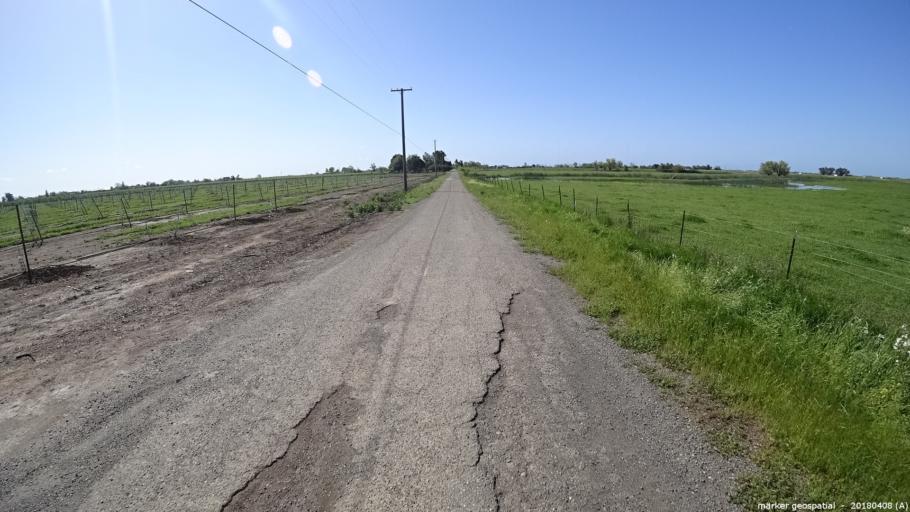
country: US
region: California
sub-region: Sacramento County
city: Laguna
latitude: 38.3454
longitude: -121.4640
